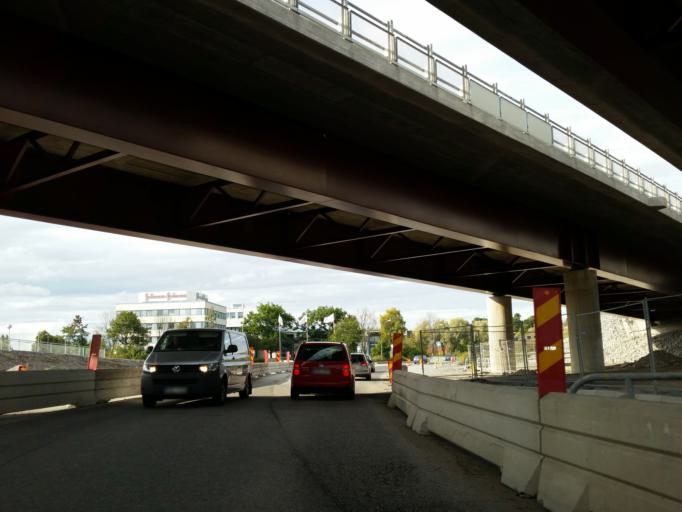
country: SE
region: Stockholm
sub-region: Upplands Vasby Kommun
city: Upplands Vaesby
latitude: 59.4749
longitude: 17.9173
